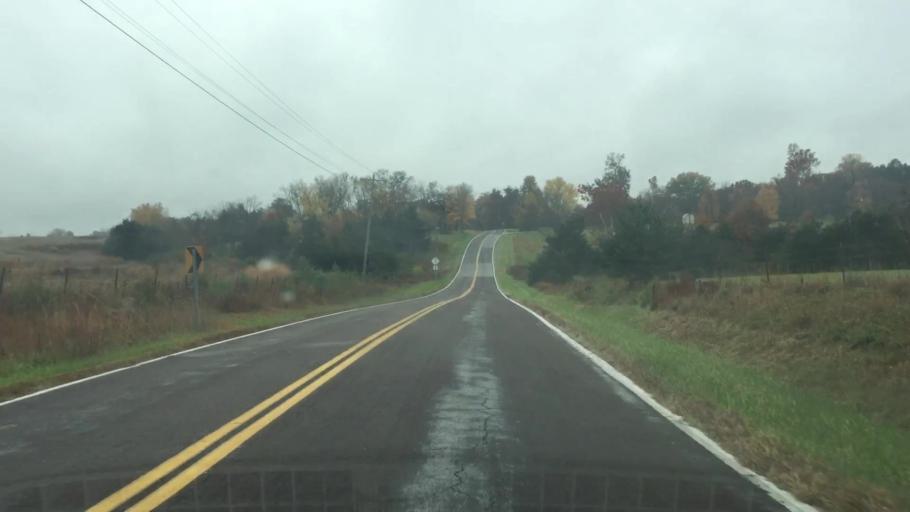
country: US
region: Missouri
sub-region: Callaway County
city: Fulton
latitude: 38.8245
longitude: -91.9083
